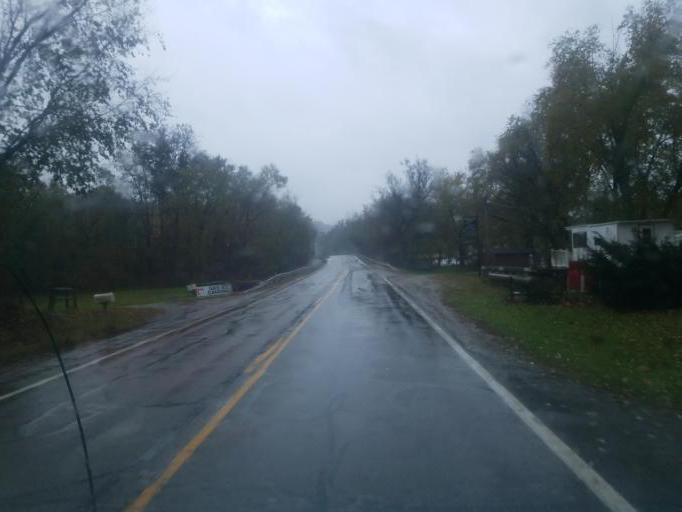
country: US
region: Ohio
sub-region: Morgan County
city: McConnelsville
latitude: 39.7757
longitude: -81.9021
